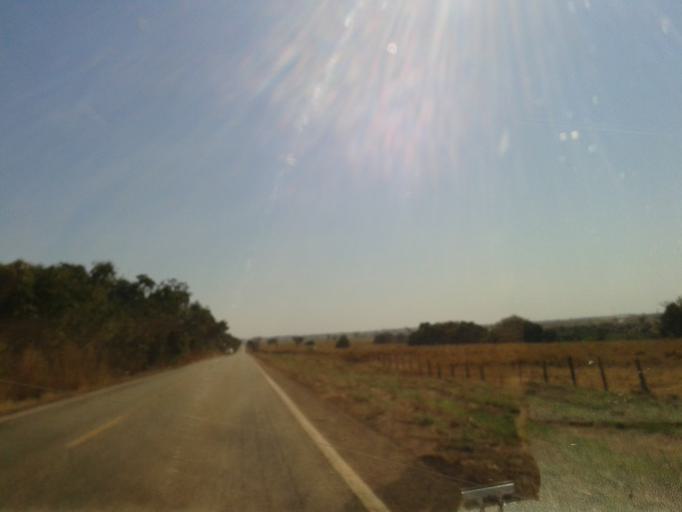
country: BR
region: Goias
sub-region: Mozarlandia
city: Mozarlandia
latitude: -14.3829
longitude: -50.4355
